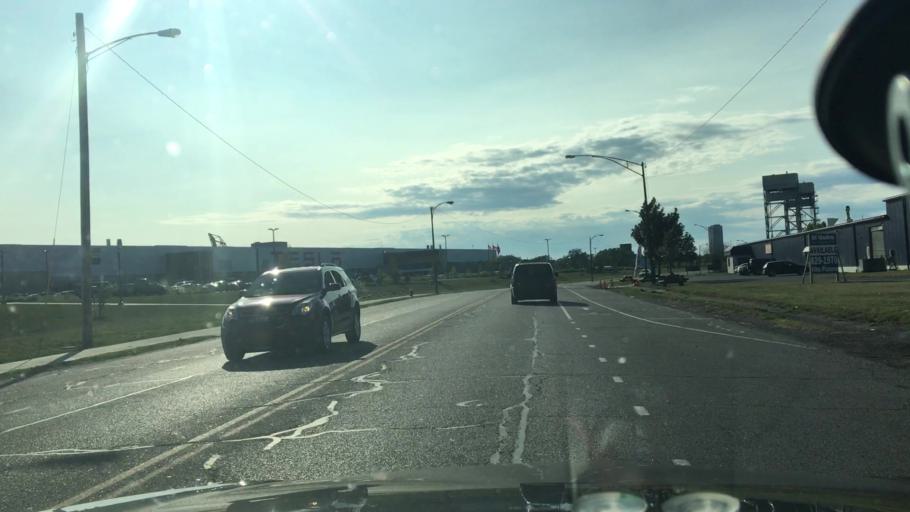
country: US
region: New York
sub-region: Erie County
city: Lackawanna
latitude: 42.8599
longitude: -78.8376
